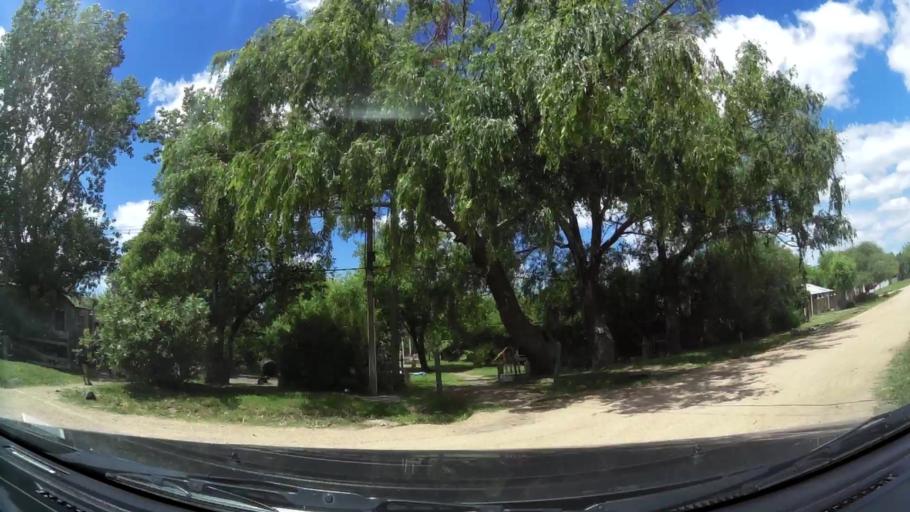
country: UY
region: Canelones
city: Colonia Nicolich
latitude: -34.8170
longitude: -55.9994
